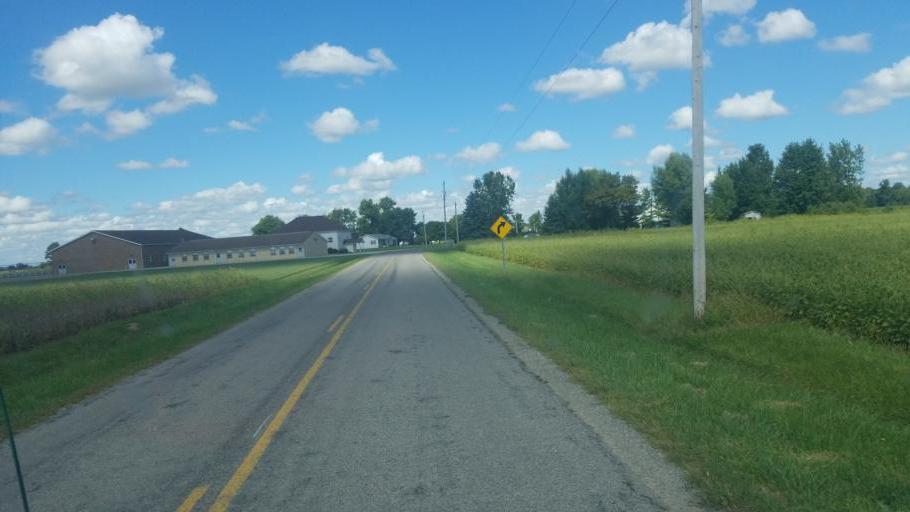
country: US
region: Ohio
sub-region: Madison County
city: Plain City
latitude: 40.0589
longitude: -83.3450
